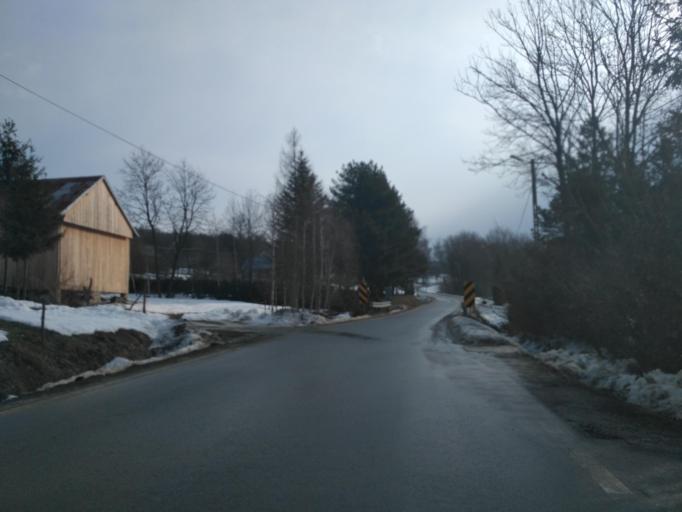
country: PL
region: Subcarpathian Voivodeship
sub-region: Powiat brzozowski
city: Dydnia
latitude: 49.6514
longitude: 22.1557
